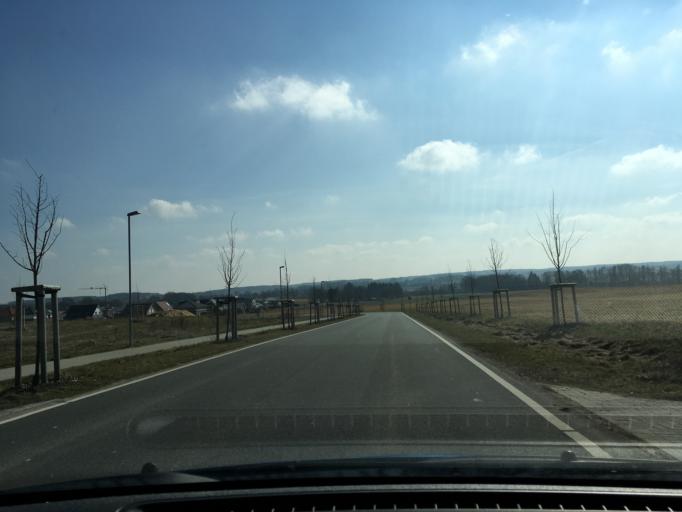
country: DE
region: Lower Saxony
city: Salzhausen
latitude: 53.2256
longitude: 10.1588
